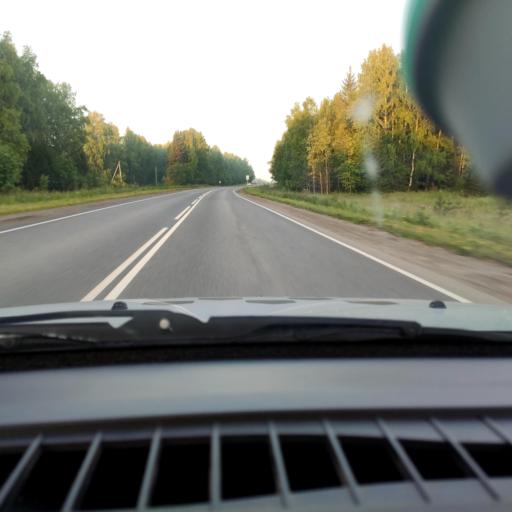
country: RU
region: Perm
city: Orda
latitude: 57.2492
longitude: 56.9974
